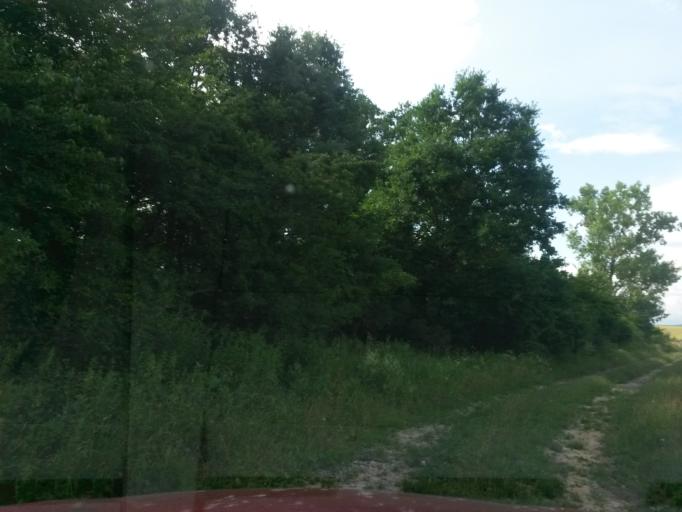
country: SK
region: Kosicky
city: Moldava nad Bodvou
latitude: 48.6215
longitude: 21.1026
